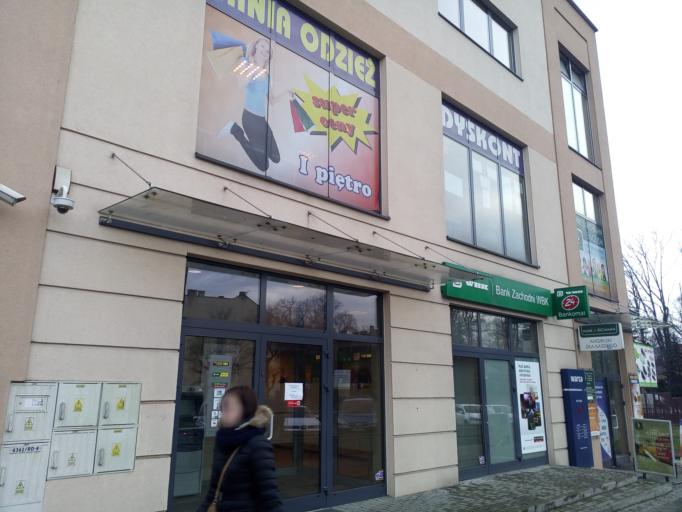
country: PL
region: Lesser Poland Voivodeship
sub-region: Powiat nowosadecki
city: Nowy Sacz
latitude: 49.6185
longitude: 20.6956
